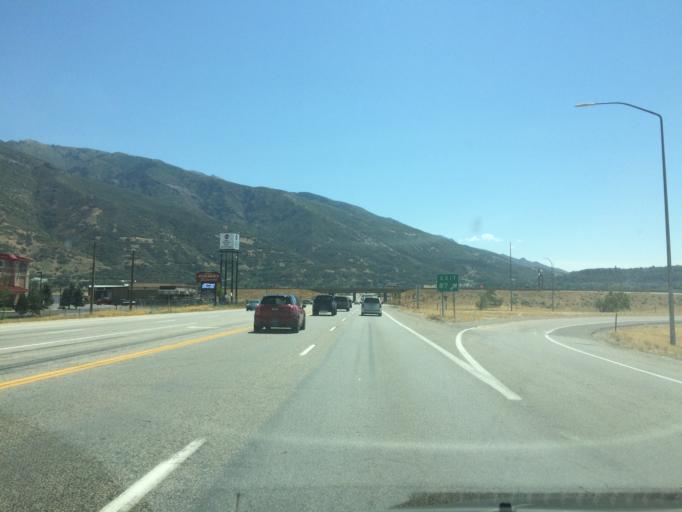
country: US
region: Utah
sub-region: Weber County
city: Uintah
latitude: 41.1400
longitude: -111.9158
